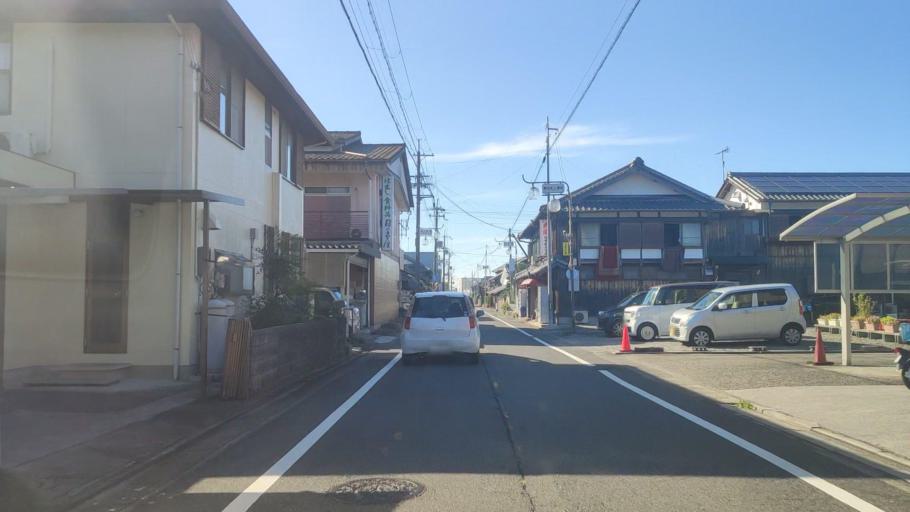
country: JP
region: Shiga Prefecture
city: Minakuchicho-matoba
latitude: 34.8882
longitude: 136.2312
